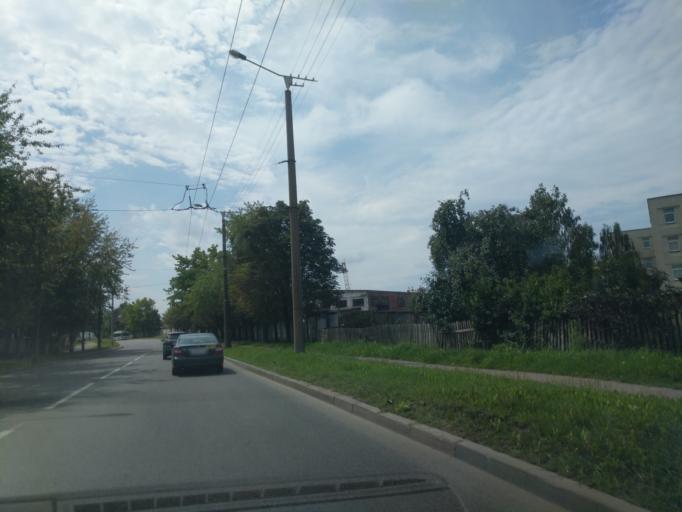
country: BY
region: Minsk
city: Novoye Medvezhino
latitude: 53.8909
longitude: 27.4827
